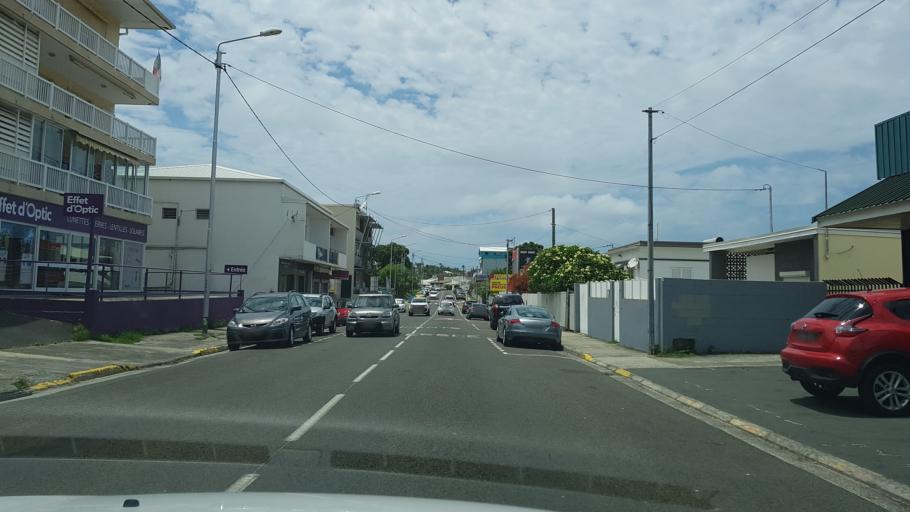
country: NC
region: South Province
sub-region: Noumea
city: Noumea
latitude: -22.2828
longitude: 166.4531
